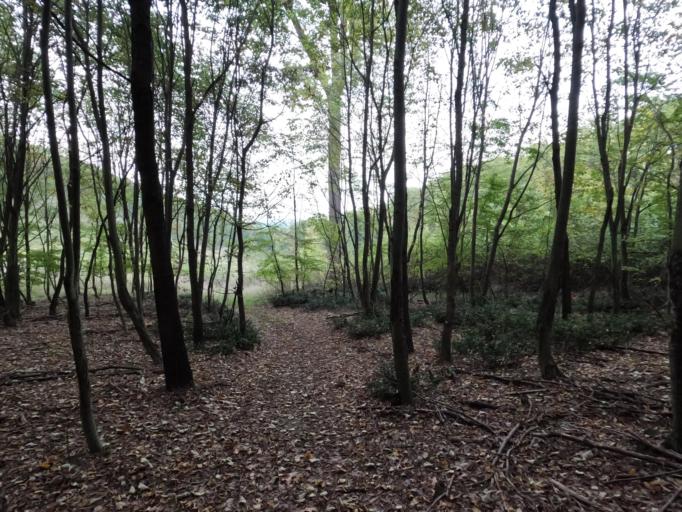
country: HU
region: Tolna
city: Szentgalpuszta
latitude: 46.3230
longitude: 18.6176
